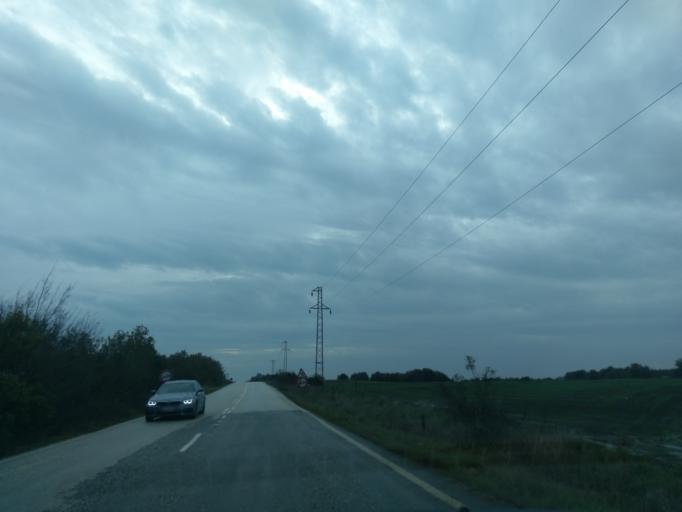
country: TR
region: Istanbul
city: Canta
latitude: 41.1762
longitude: 28.0901
